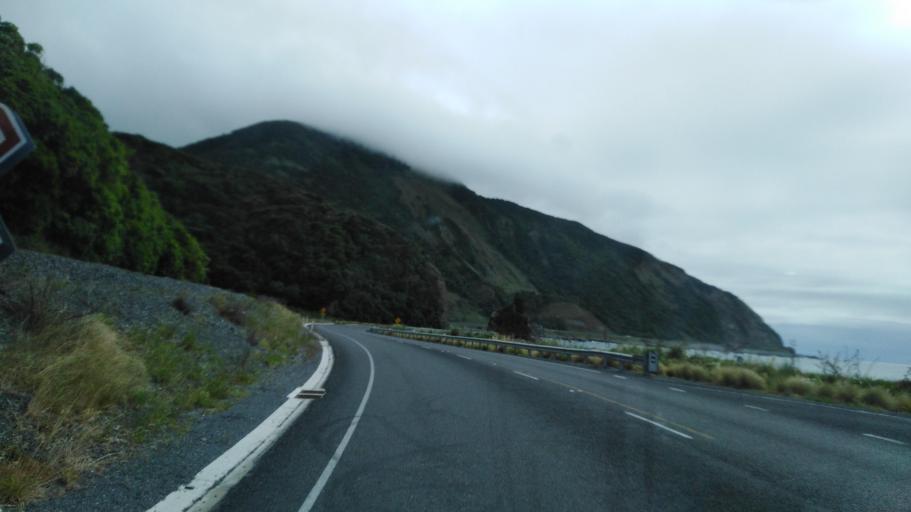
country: NZ
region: Canterbury
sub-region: Kaikoura District
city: Kaikoura
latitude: -42.2612
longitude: 173.8104
